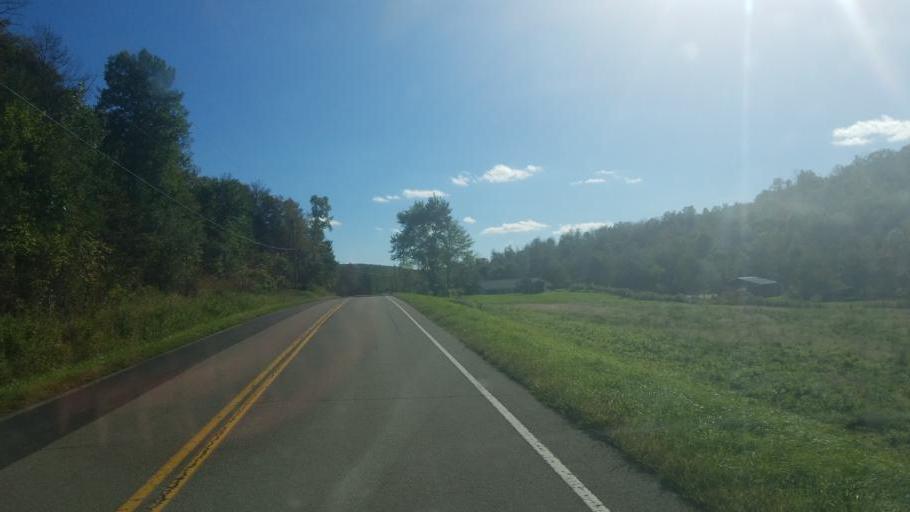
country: US
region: New York
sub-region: Allegany County
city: Friendship
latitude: 42.2948
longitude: -78.1177
